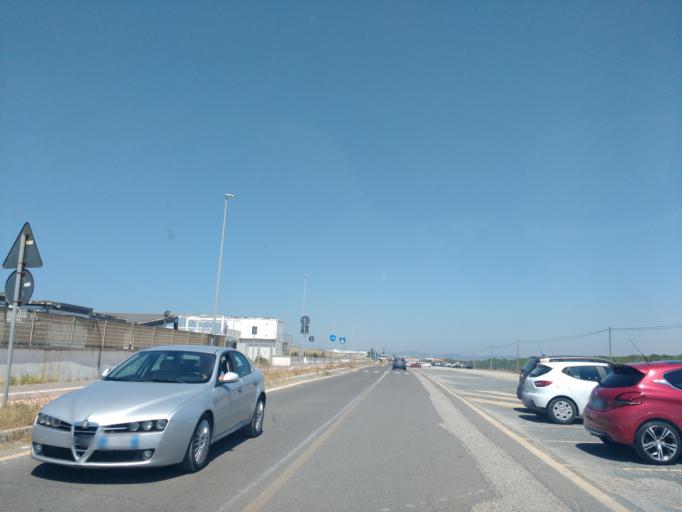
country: IT
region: Latium
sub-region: Citta metropolitana di Roma Capitale
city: Passo Oscuro
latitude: 41.8832
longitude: 12.1724
